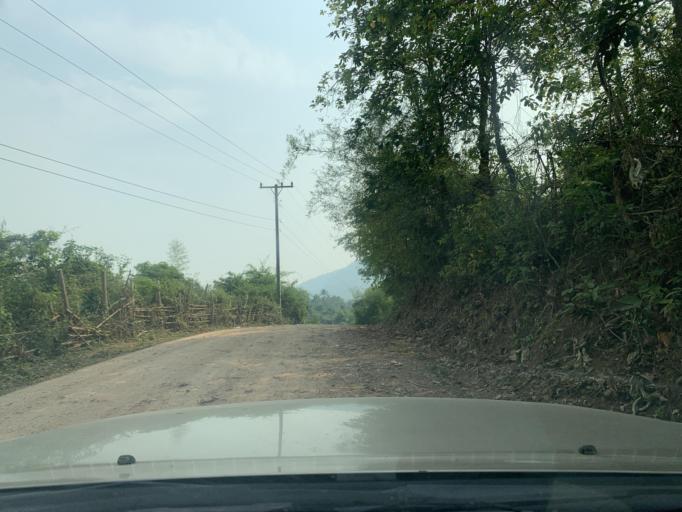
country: LA
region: Louangphabang
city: Louangphabang
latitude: 19.9083
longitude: 102.1327
